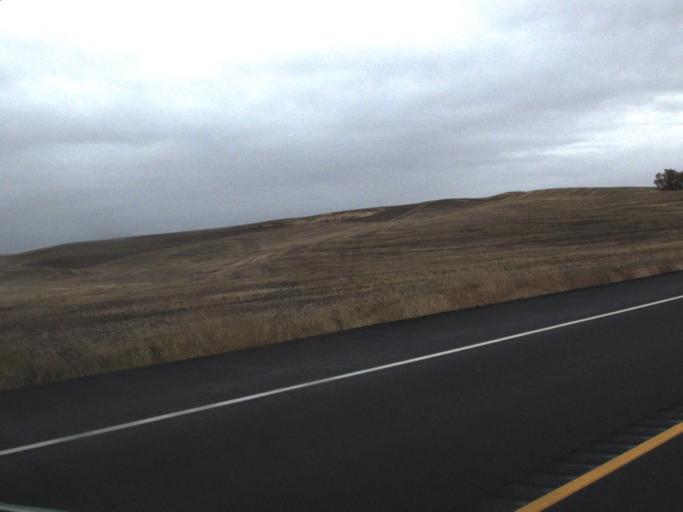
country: US
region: Washington
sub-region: Whitman County
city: Pullman
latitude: 46.7647
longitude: -117.2665
